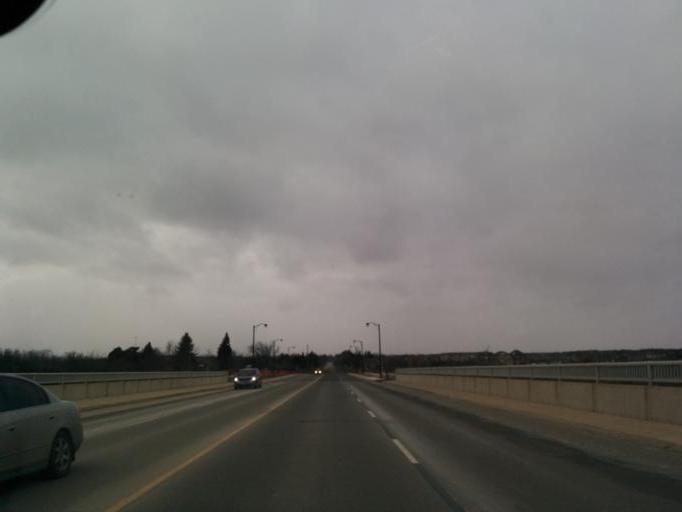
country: CA
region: Ontario
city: Brampton
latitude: 43.7475
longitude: -79.8196
